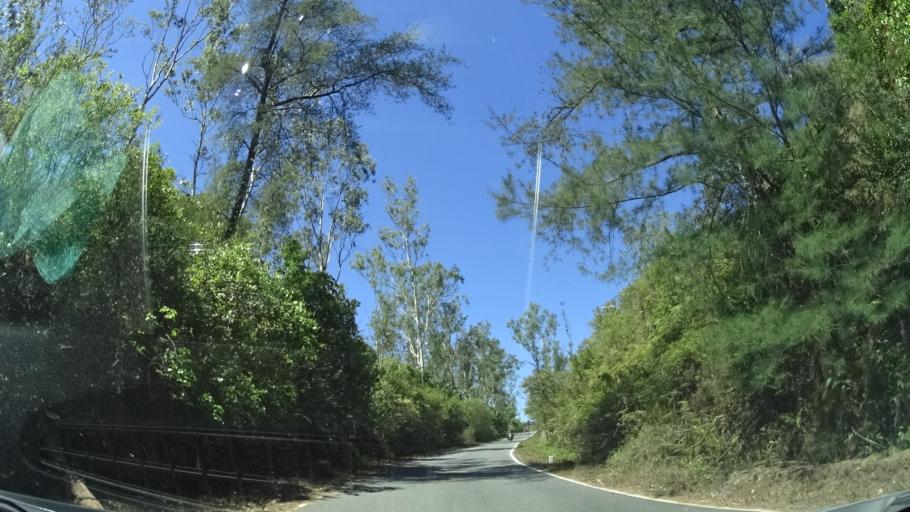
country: IN
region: Karnataka
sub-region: Chikmagalur
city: Sringeri
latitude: 13.2110
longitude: 75.2105
